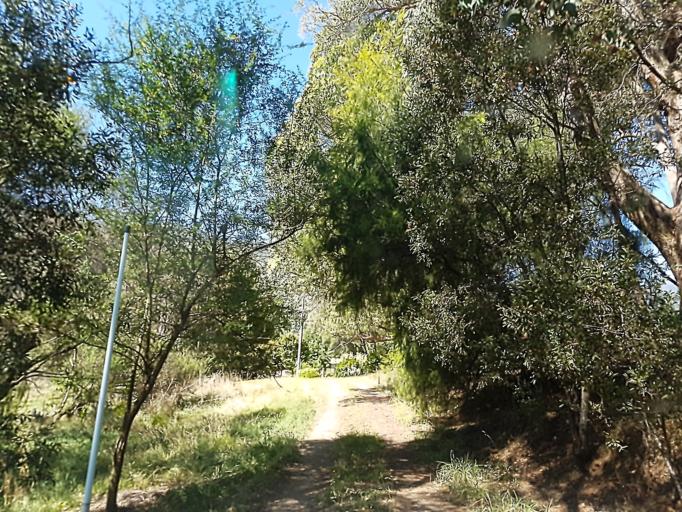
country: AU
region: Victoria
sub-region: Alpine
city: Mount Beauty
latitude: -36.8215
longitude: 147.0627
